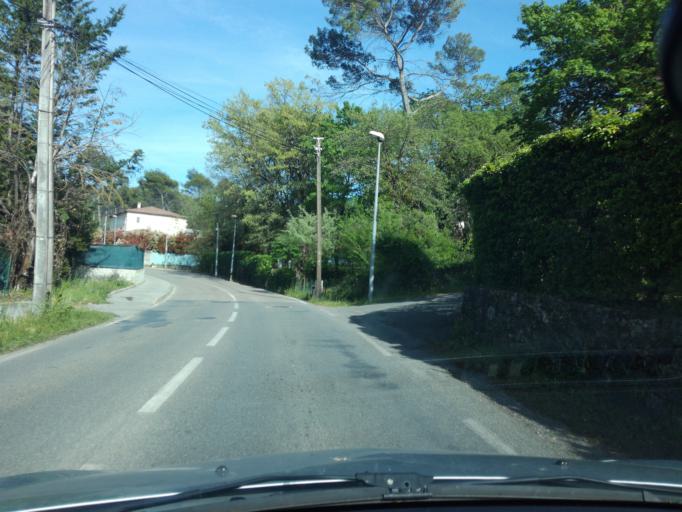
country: FR
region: Provence-Alpes-Cote d'Azur
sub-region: Departement des Alpes-Maritimes
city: La Roquette-sur-Siagne
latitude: 43.6204
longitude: 6.9515
